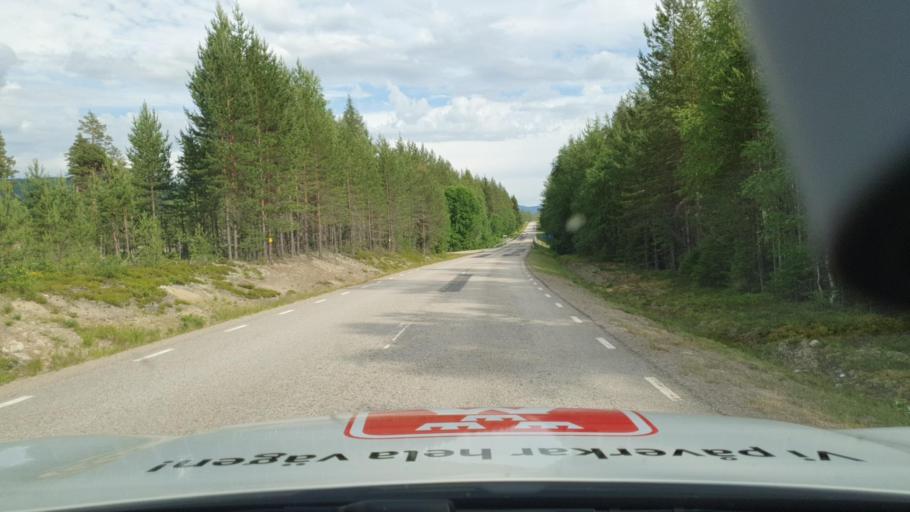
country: NO
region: Hedmark
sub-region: Trysil
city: Innbygda
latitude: 60.9288
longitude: 12.5100
